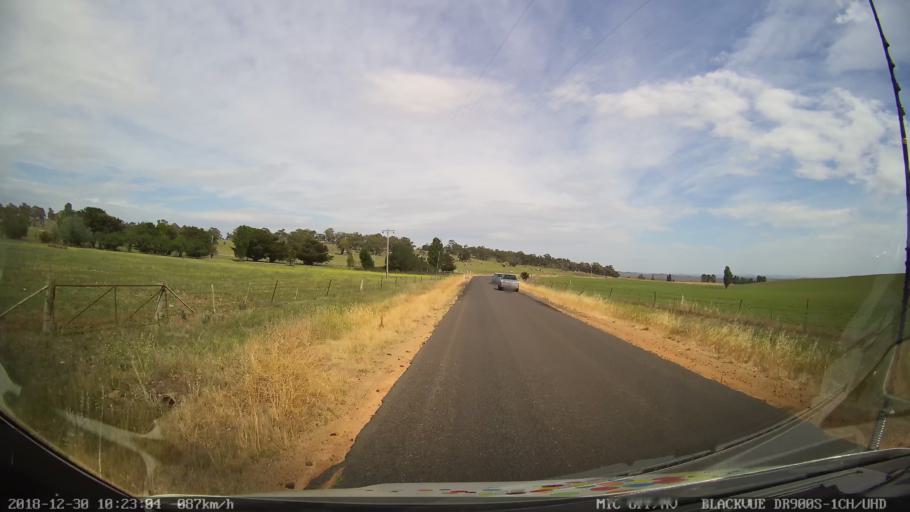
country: AU
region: New South Wales
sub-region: Snowy River
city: Berridale
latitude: -36.5411
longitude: 148.9855
